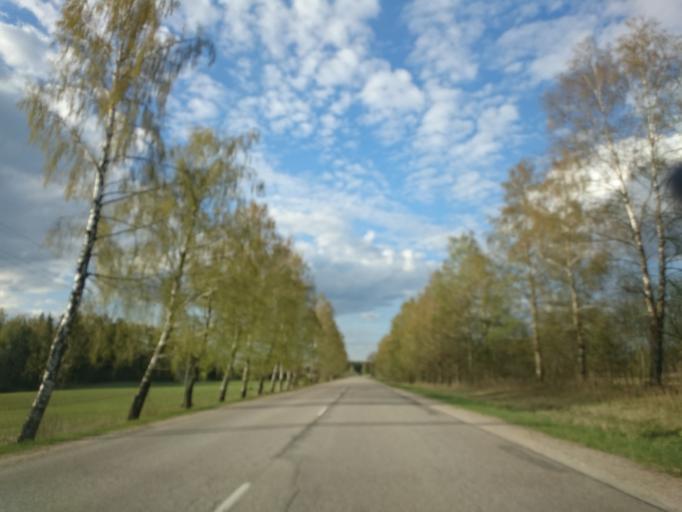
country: LV
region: Kuldigas Rajons
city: Kuldiga
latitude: 56.8958
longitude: 21.8880
